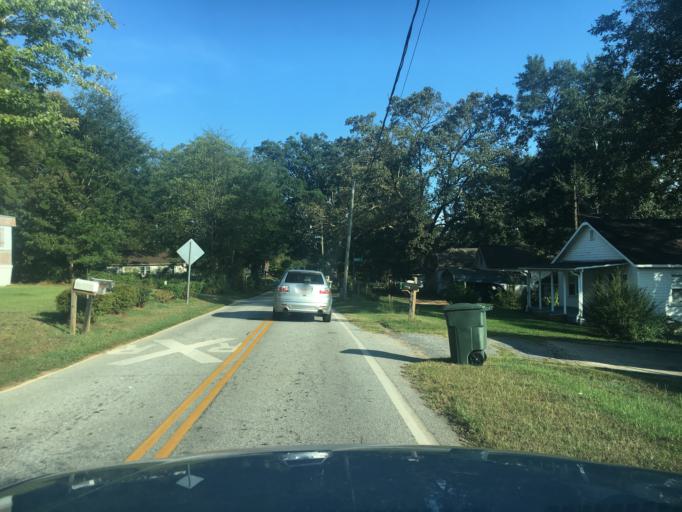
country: US
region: South Carolina
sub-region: Oconee County
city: Westminster
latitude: 34.6615
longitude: -83.0829
